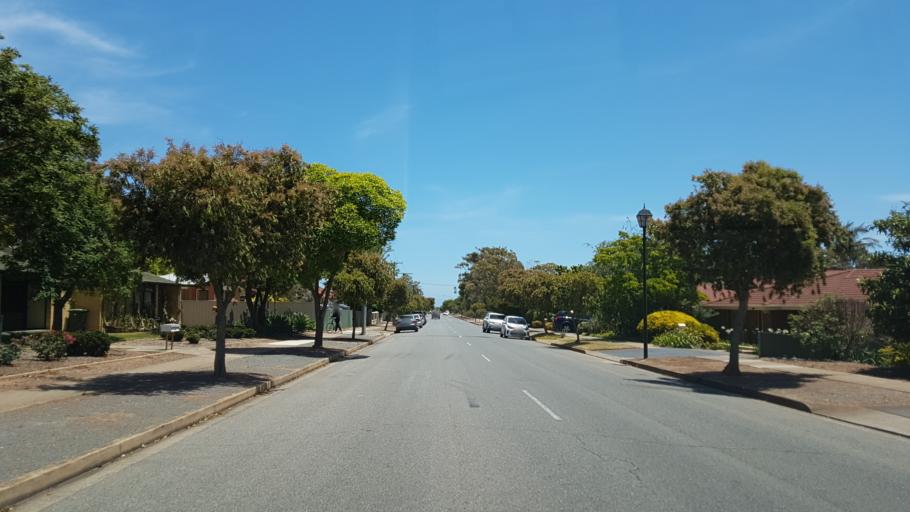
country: AU
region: South Australia
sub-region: Holdfast Bay
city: Seacliff Park
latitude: -35.0255
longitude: 138.5368
